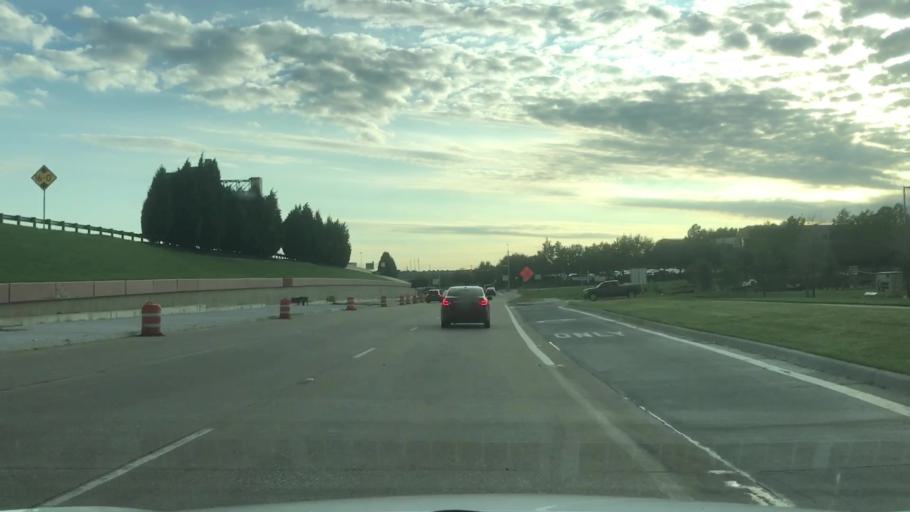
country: US
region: Texas
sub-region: Dallas County
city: Coppell
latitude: 32.8913
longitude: -96.9801
